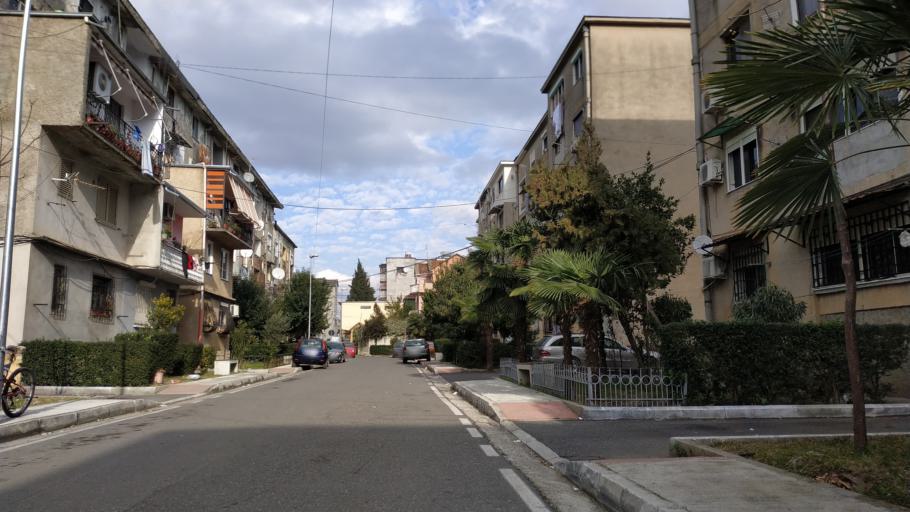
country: AL
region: Shkoder
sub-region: Rrethi i Shkodres
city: Shkoder
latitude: 42.0599
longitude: 19.5046
